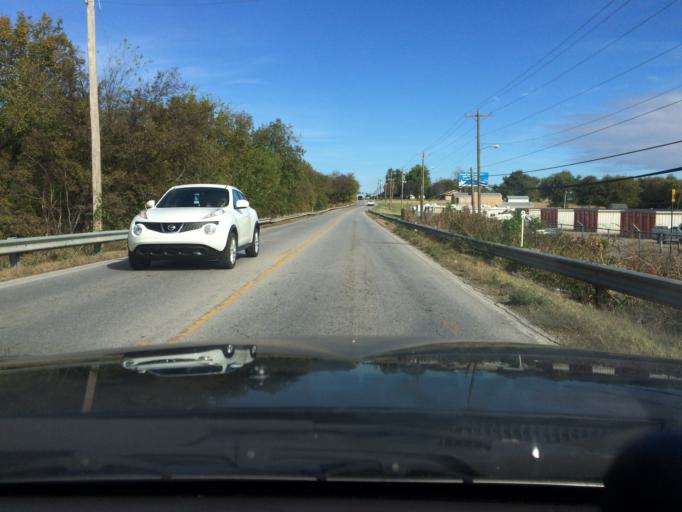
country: US
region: Oklahoma
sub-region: Tulsa County
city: Broken Arrow
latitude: 36.0860
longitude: -95.7617
